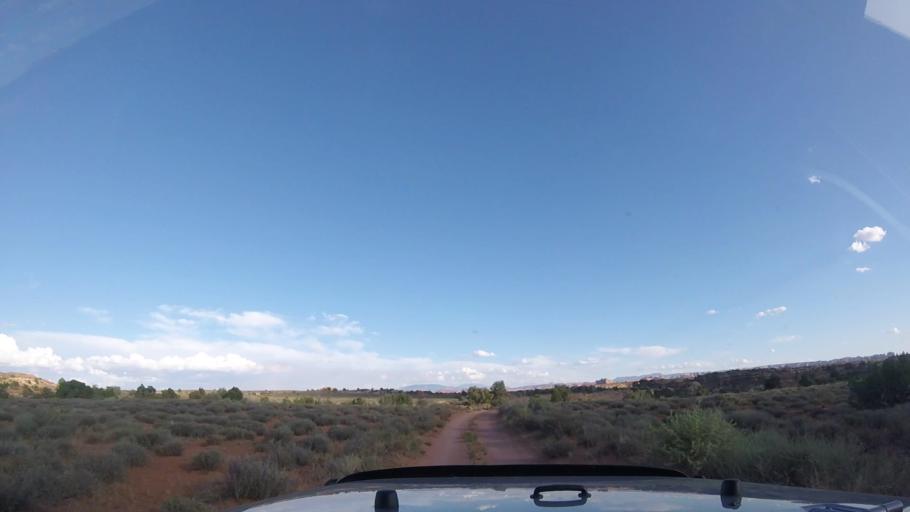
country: US
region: Utah
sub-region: Grand County
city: Moab
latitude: 38.2062
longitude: -109.7858
